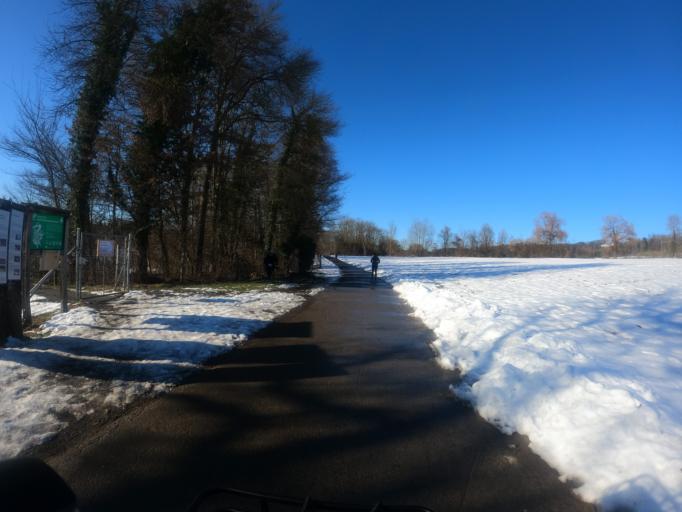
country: CH
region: Aargau
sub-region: Bezirk Bremgarten
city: Unterlunkhofen
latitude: 47.3259
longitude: 8.3735
